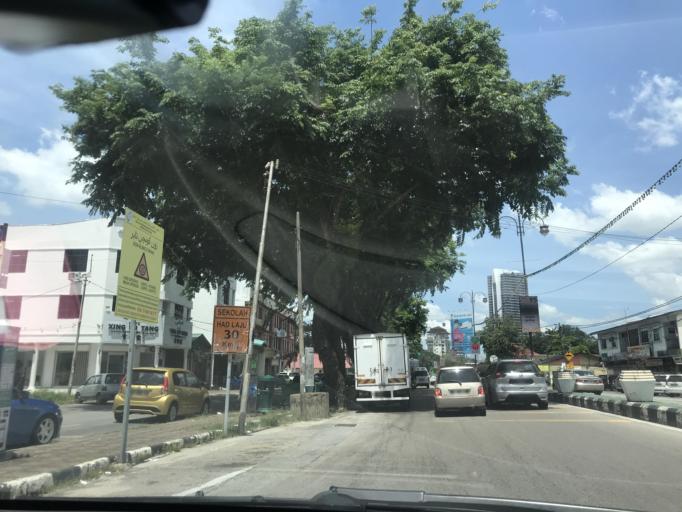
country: MY
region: Kelantan
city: Kota Bharu
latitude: 6.1272
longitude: 102.2422
